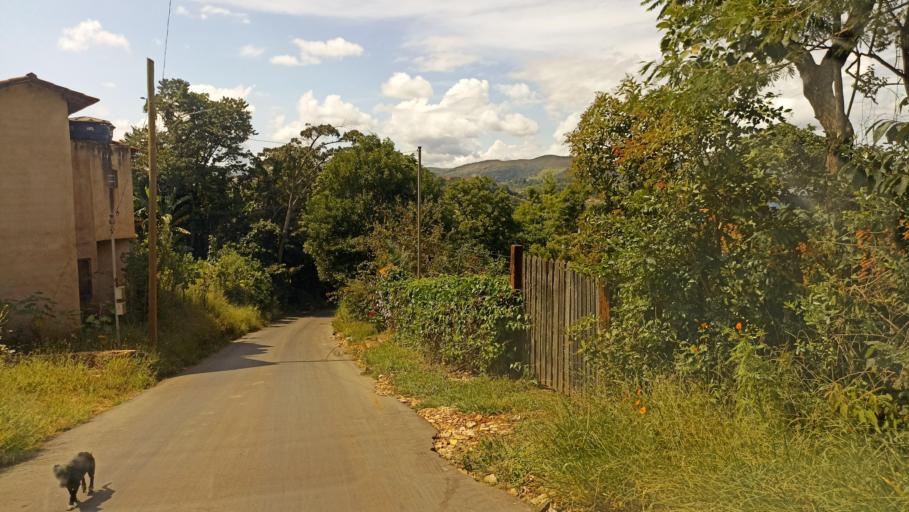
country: BR
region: Minas Gerais
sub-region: Itabirito
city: Itabirito
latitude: -20.3532
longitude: -43.7206
